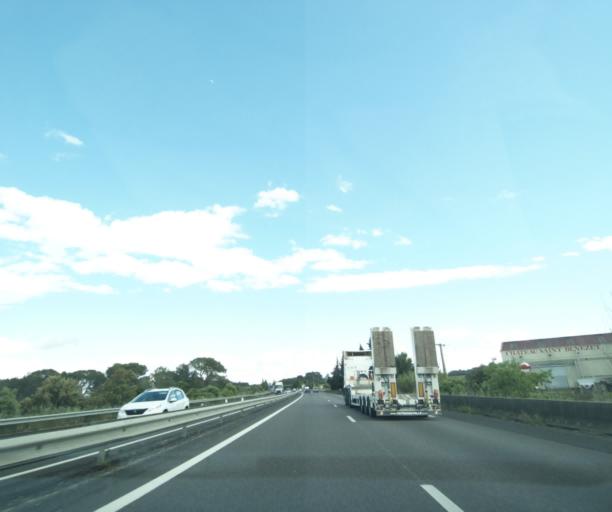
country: FR
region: Languedoc-Roussillon
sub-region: Departement du Gard
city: Garons
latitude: 43.7463
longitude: 4.4378
